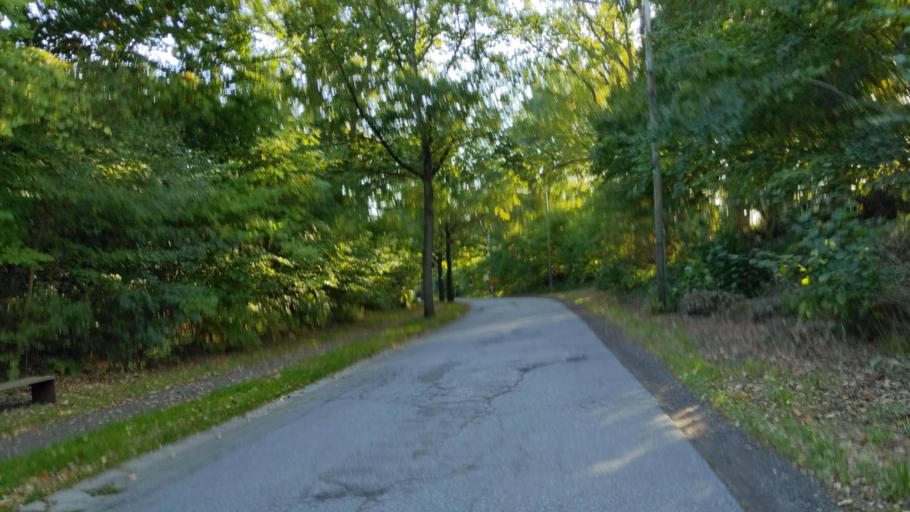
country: DE
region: Schleswig-Holstein
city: Susel
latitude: 54.0841
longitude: 10.6835
